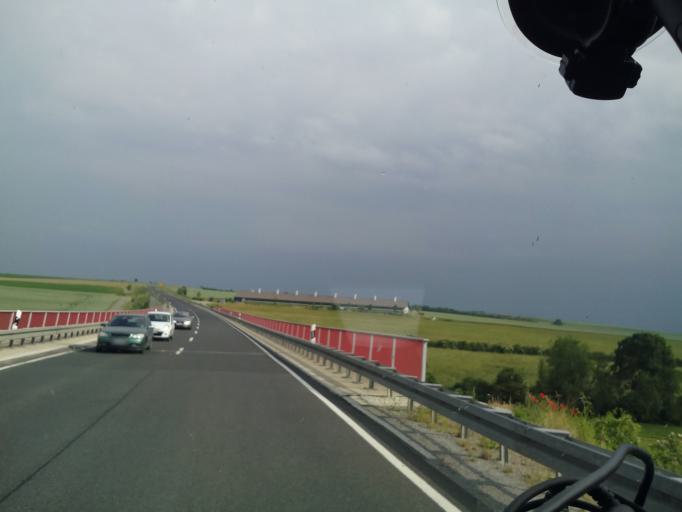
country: DE
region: Bavaria
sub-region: Regierungsbezirk Unterfranken
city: Mellrichstadt
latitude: 50.4322
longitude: 10.3276
